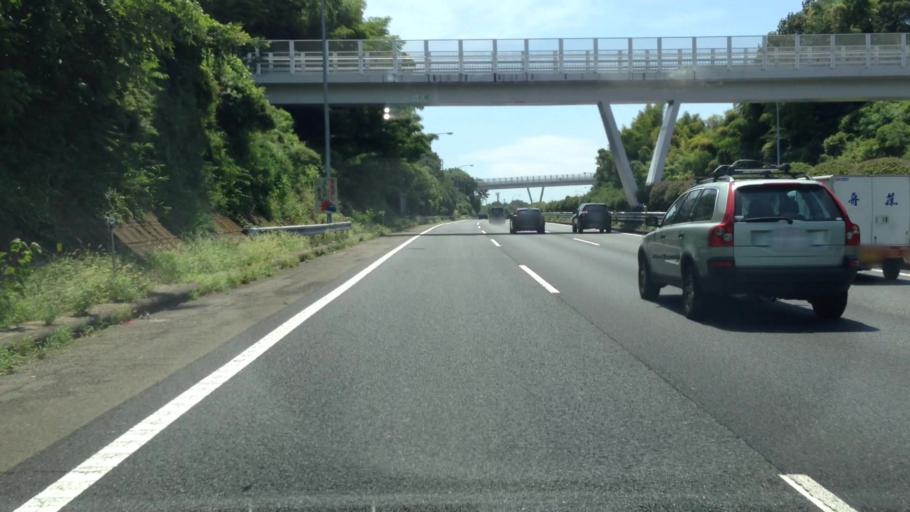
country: JP
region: Kanagawa
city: Yokohama
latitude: 35.5069
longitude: 139.5931
